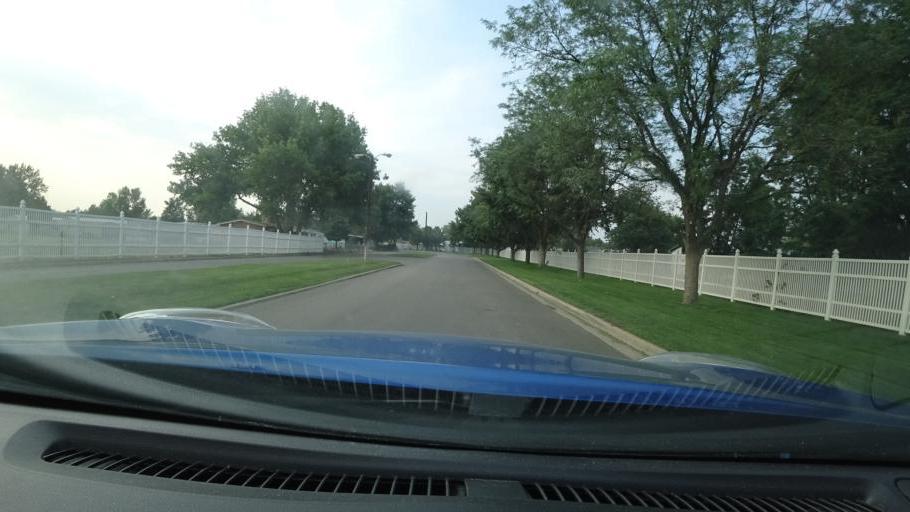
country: US
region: Colorado
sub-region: Adams County
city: Aurora
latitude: 39.7408
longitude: -104.7868
